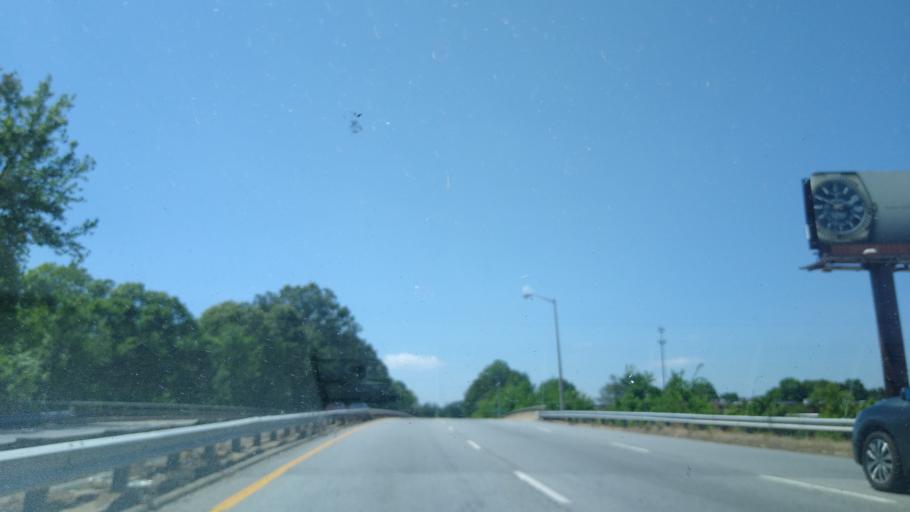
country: US
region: North Carolina
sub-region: Guilford County
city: Greensboro
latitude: 36.0881
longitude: -79.8102
